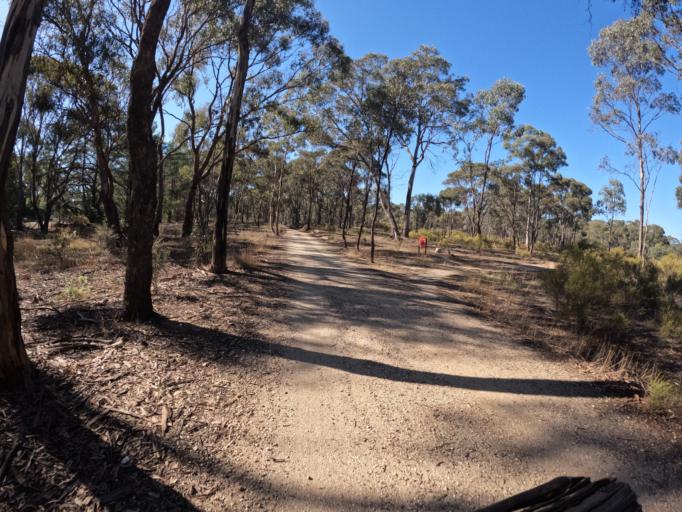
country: AU
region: Victoria
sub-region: Greater Bendigo
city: Kennington
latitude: -36.7772
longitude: 144.3648
